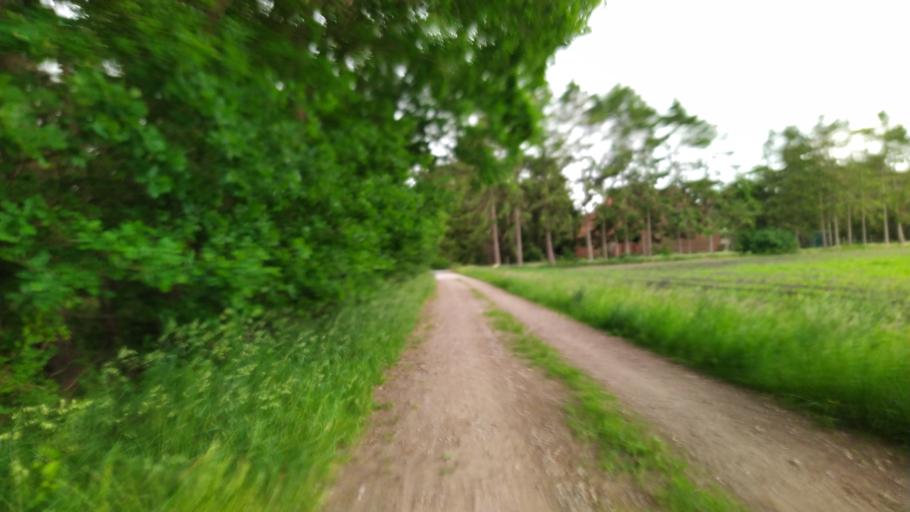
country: DE
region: Lower Saxony
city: Farven
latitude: 53.4303
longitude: 9.2743
